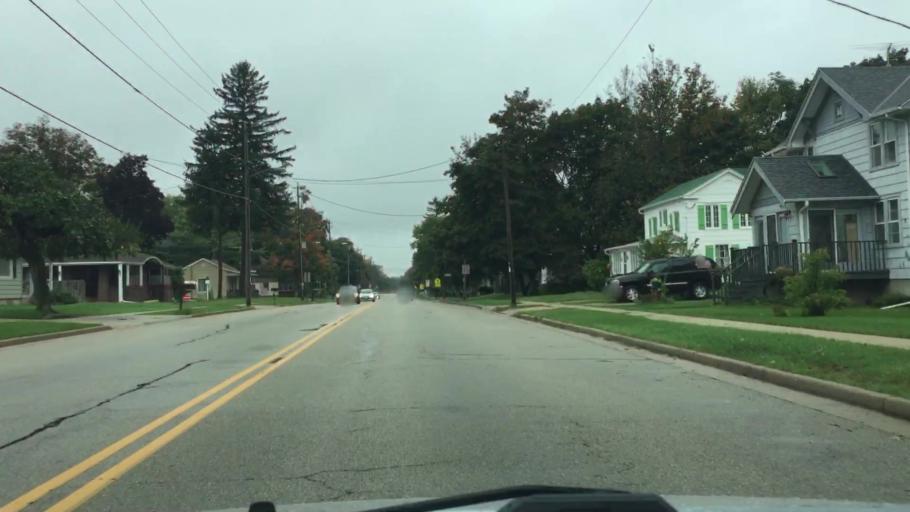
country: US
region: Wisconsin
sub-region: Jefferson County
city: Palmyra
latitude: 42.8789
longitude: -88.5879
